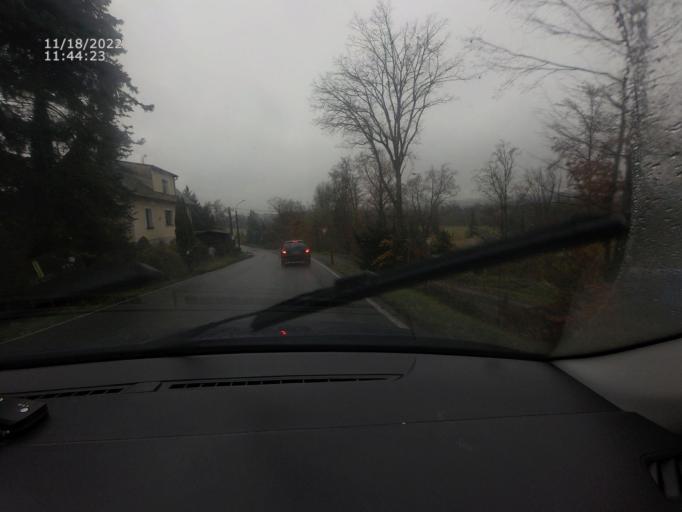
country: CZ
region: Plzensky
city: St'ahlavy
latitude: 49.6827
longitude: 13.5097
